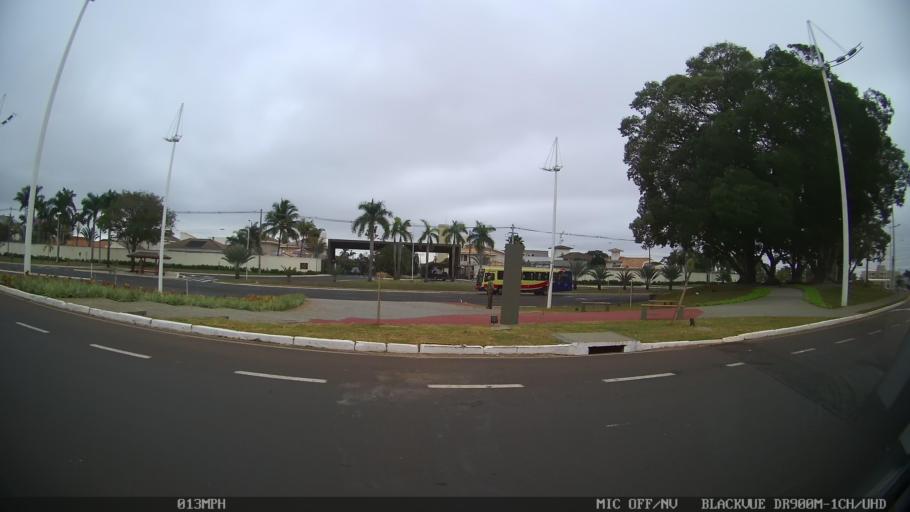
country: BR
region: Sao Paulo
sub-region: Sao Jose Do Rio Preto
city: Sao Jose do Rio Preto
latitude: -20.8462
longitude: -49.4028
